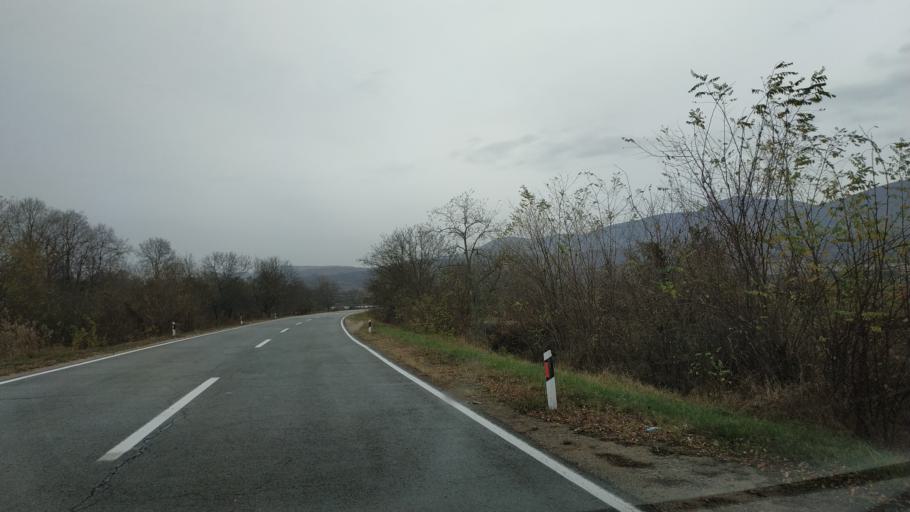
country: RS
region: Central Serbia
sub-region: Pirotski Okrug
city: Bela Palanka
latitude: 43.2296
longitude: 22.3258
